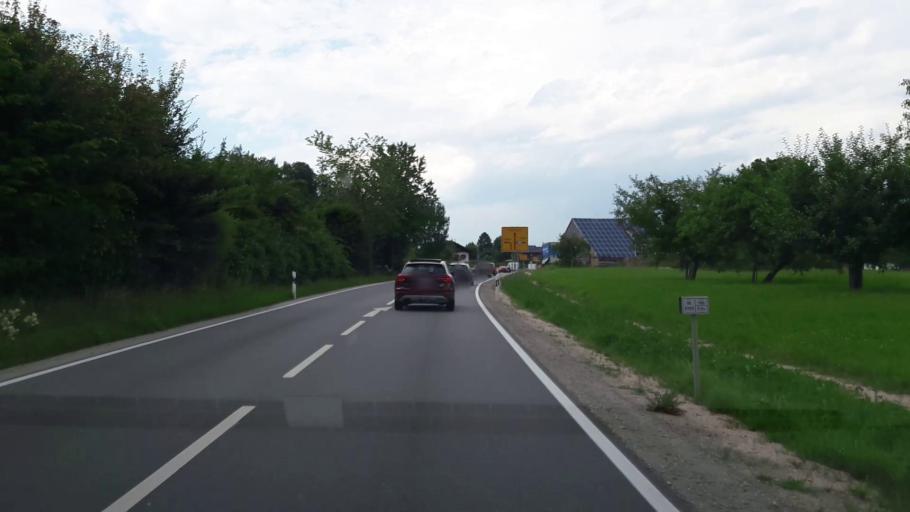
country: DE
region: Bavaria
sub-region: Upper Bavaria
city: Anger
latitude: 47.7982
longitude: 12.8664
